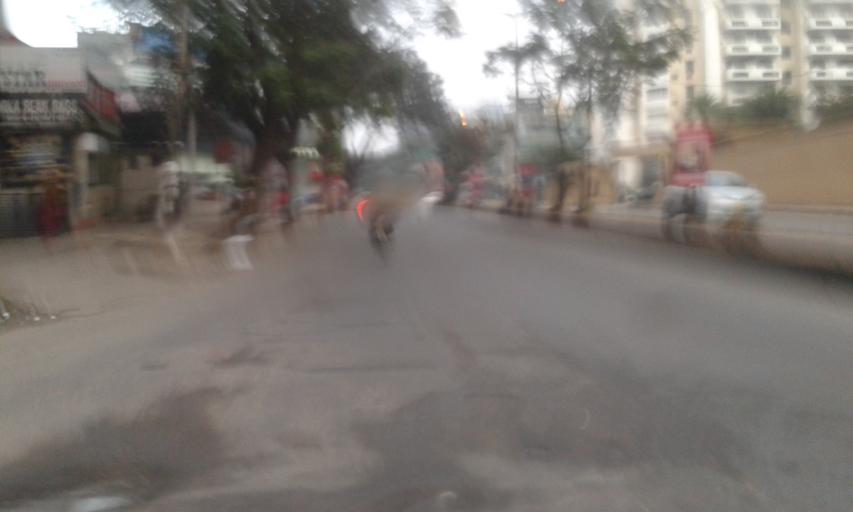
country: IN
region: Karnataka
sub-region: Bangalore Urban
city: Bangalore
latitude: 12.9342
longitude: 77.6104
